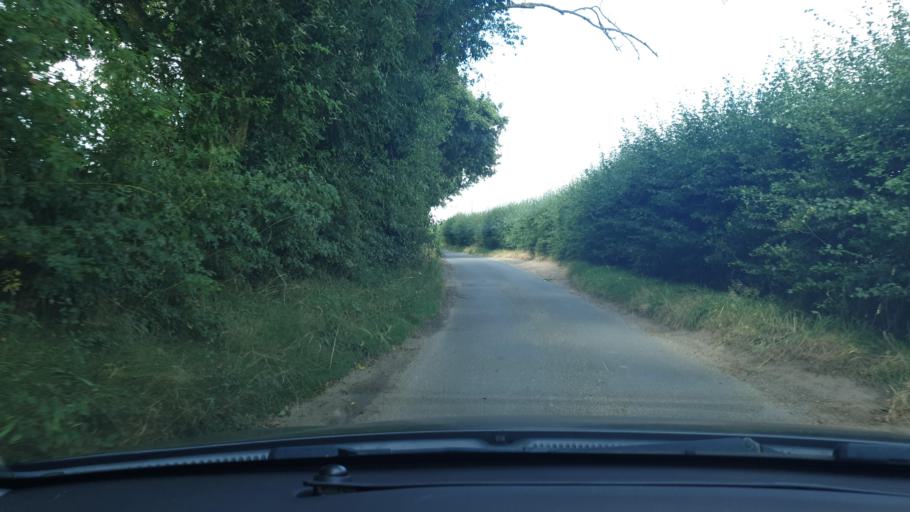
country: GB
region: England
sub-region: Suffolk
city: East Bergholt
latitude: 51.9212
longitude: 1.0002
